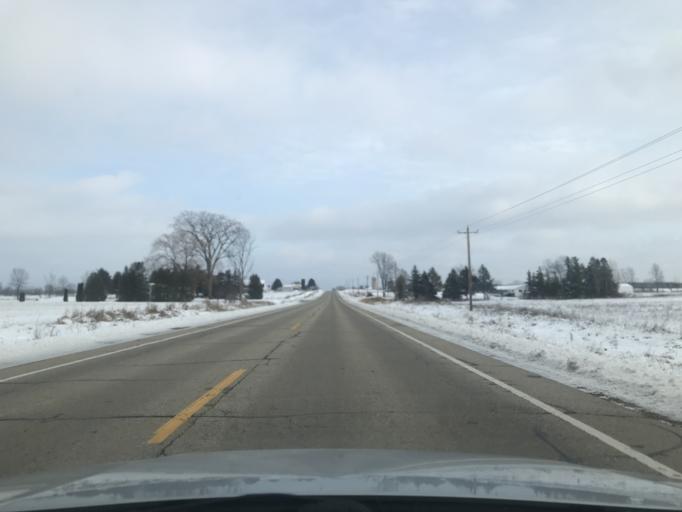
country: US
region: Wisconsin
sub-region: Oconto County
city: Oconto
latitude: 44.8934
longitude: -87.9921
